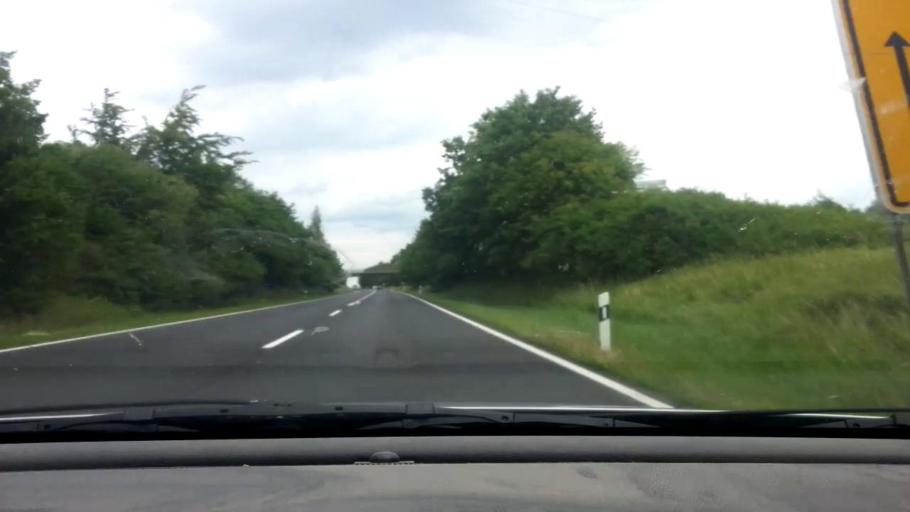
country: DE
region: Bavaria
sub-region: Upper Palatinate
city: Leonberg
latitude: 49.9752
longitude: 12.2685
